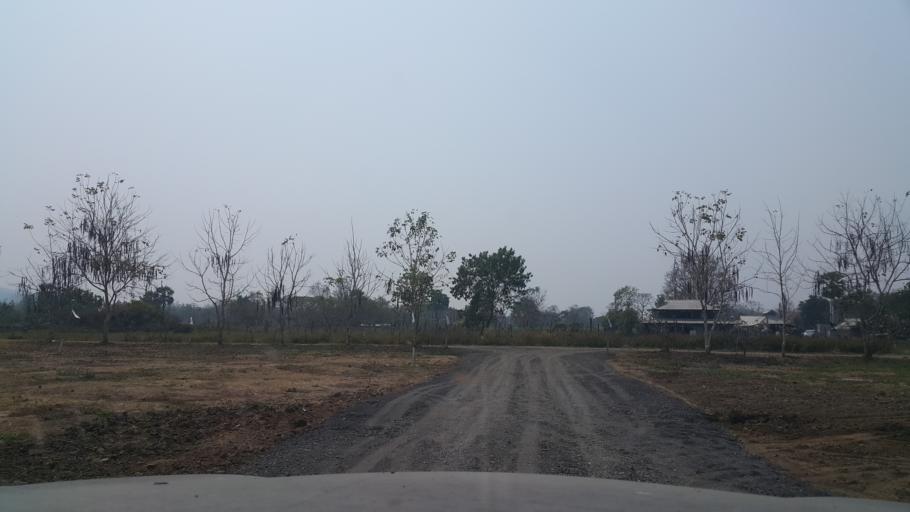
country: TH
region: Chiang Mai
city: Mae On
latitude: 18.7407
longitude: 99.2163
